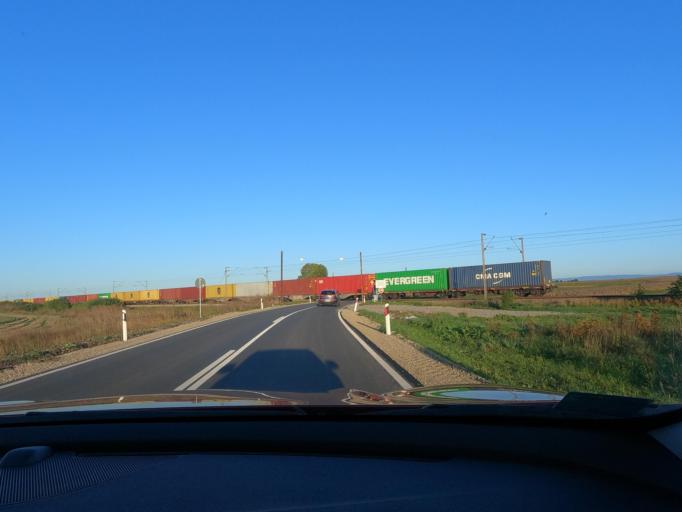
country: RS
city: Putinci
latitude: 44.9901
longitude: 19.9968
